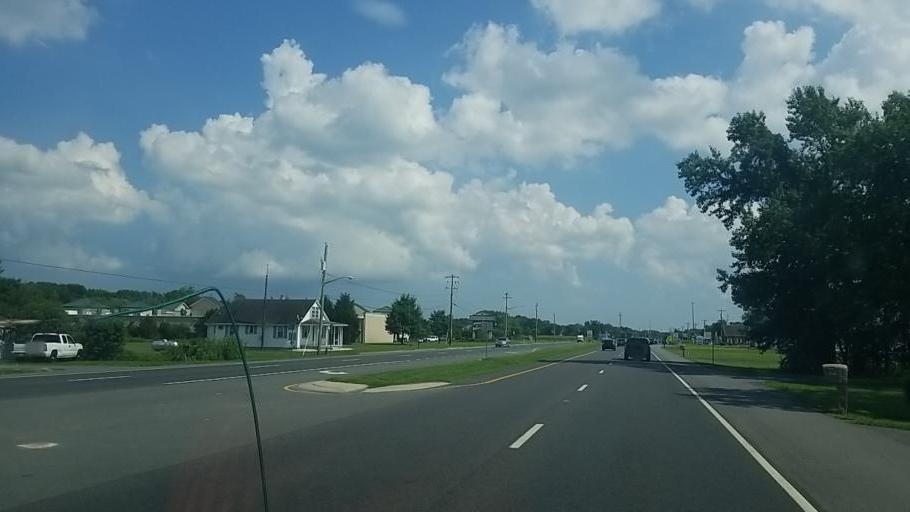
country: US
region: Delaware
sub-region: Sussex County
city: Millsboro
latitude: 38.5475
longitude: -75.2623
